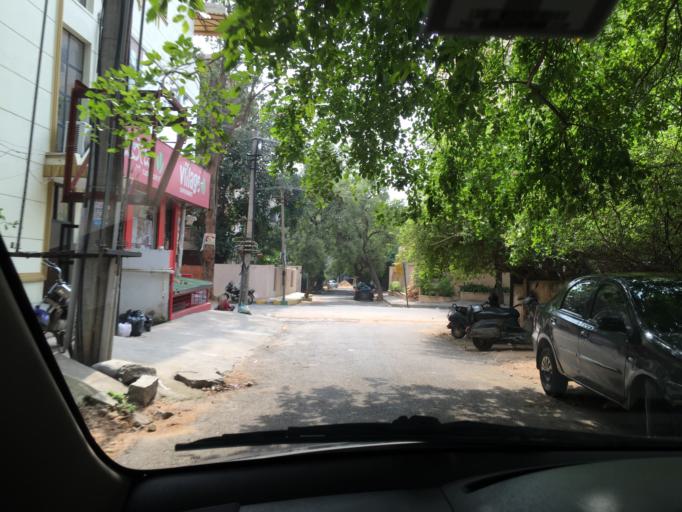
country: IN
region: Karnataka
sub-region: Bangalore Urban
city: Bangalore
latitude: 12.9996
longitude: 77.6234
